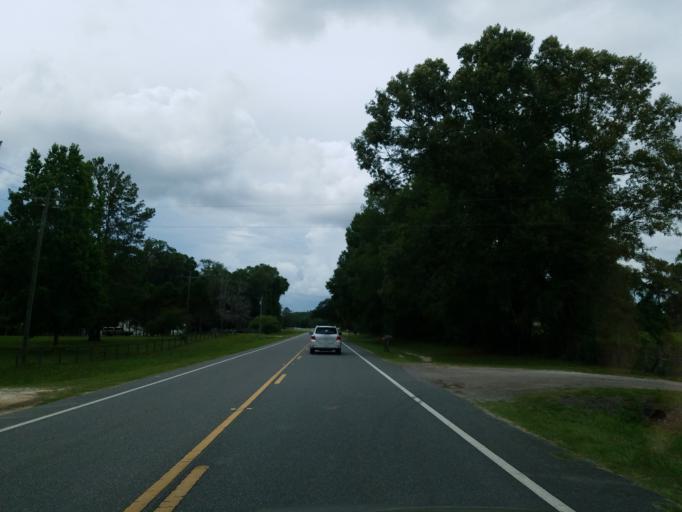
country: US
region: Florida
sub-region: Alachua County
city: High Springs
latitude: 29.9115
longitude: -82.5031
